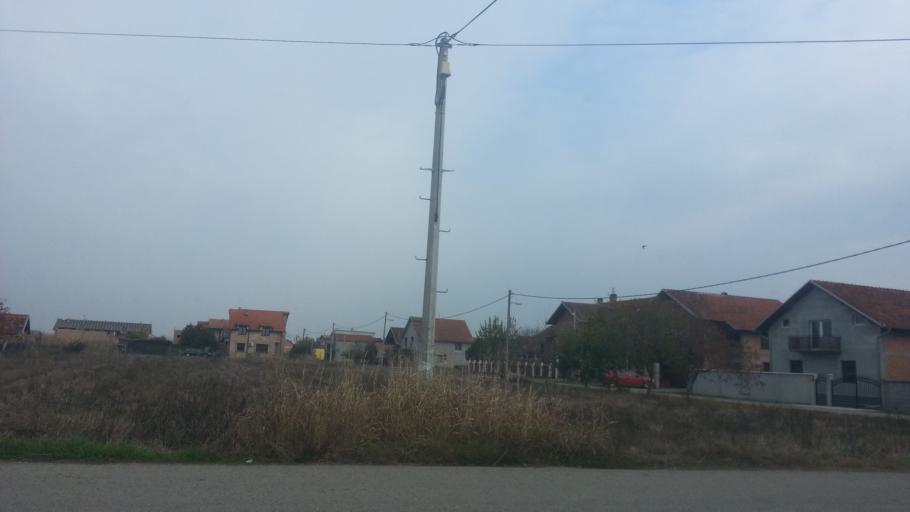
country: RS
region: Autonomna Pokrajina Vojvodina
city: Nova Pazova
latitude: 44.9565
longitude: 20.2107
